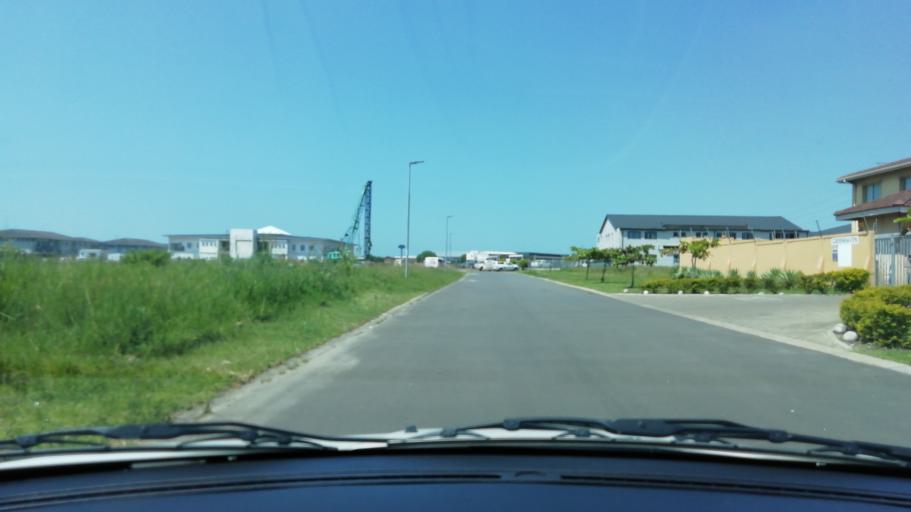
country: ZA
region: KwaZulu-Natal
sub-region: uThungulu District Municipality
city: Richards Bay
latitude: -28.7406
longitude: 32.0507
